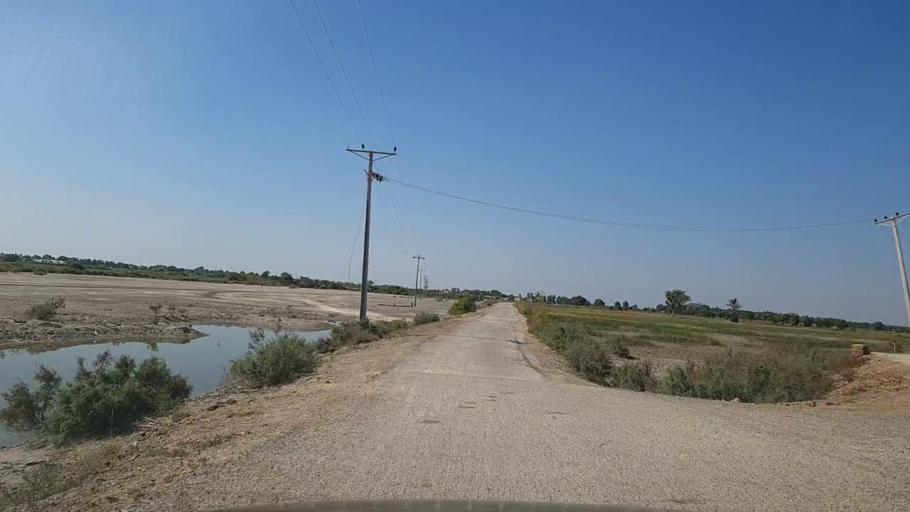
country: PK
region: Sindh
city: Mirpur Sakro
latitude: 24.6086
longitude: 67.7851
